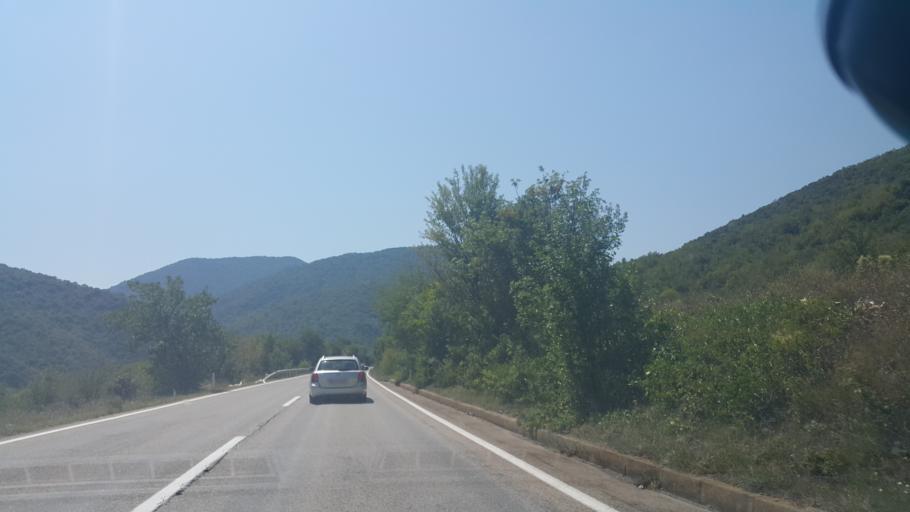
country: MK
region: Gevgelija
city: Miravci
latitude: 41.3783
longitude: 22.3946
